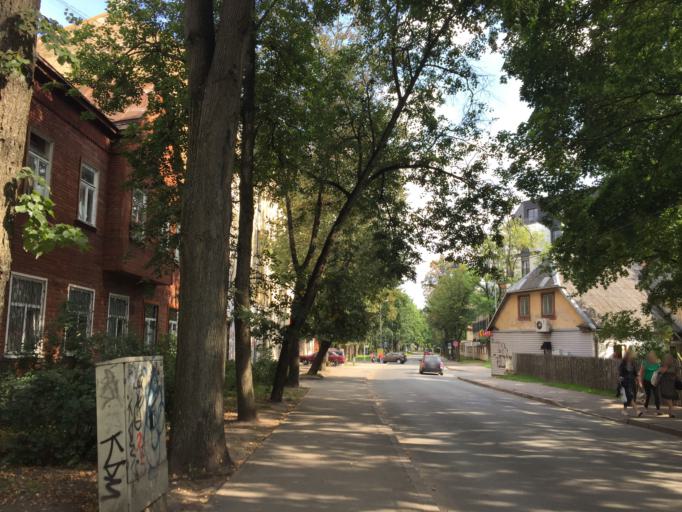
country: LV
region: Riga
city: Riga
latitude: 56.9341
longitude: 24.0759
